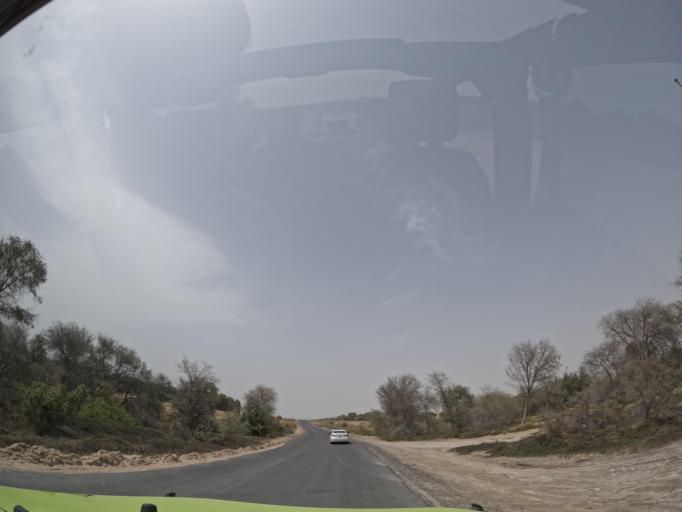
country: AE
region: Dubai
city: Dubai
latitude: 25.1410
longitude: 55.3406
